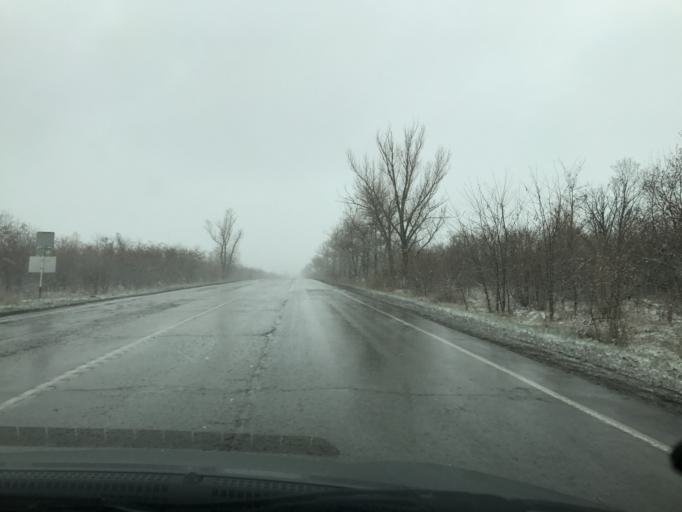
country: RU
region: Rostov
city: Kirovskaya
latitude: 47.0232
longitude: 39.8939
